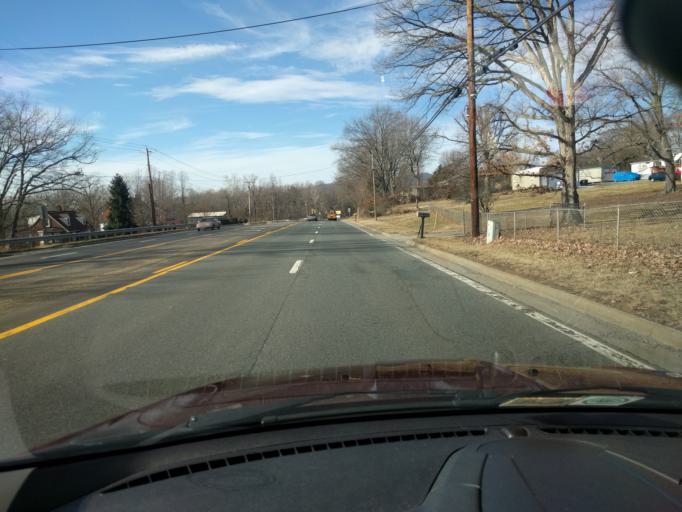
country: US
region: Virginia
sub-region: Amherst County
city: Madison Heights
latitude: 37.4856
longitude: -79.1203
